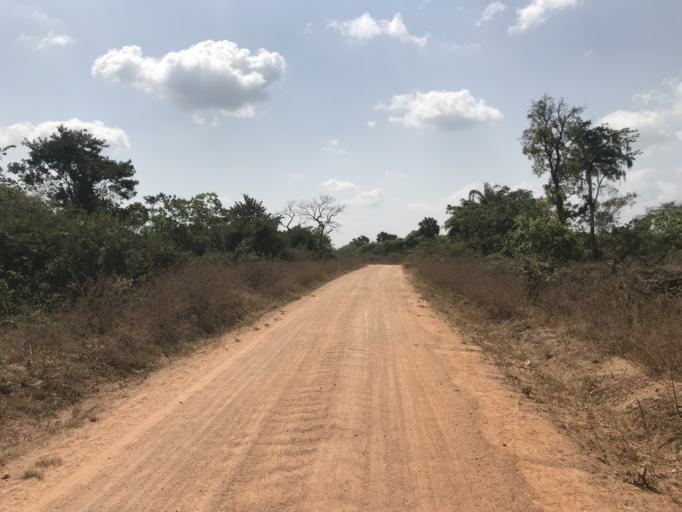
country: NG
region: Osun
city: Ifon
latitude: 7.9446
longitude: 4.4906
